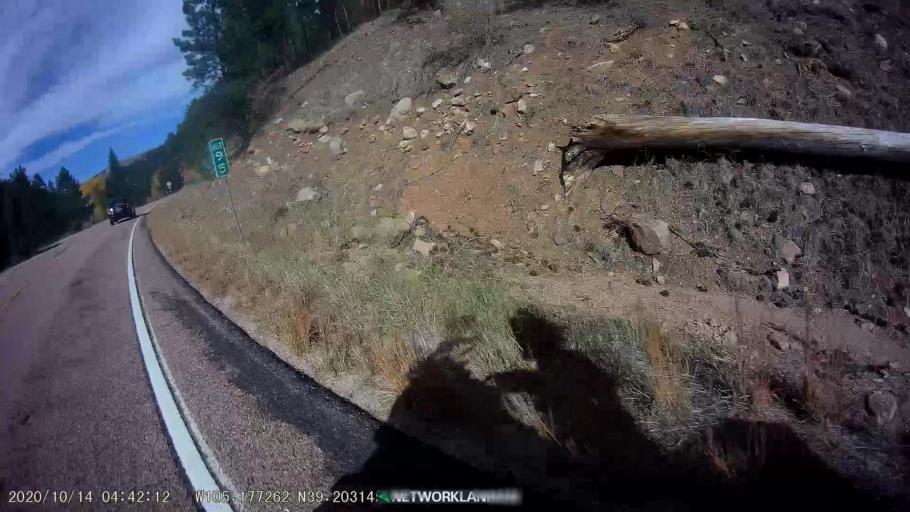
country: US
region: Colorado
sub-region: Douglas County
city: Perry Park
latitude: 39.2032
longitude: -105.1773
